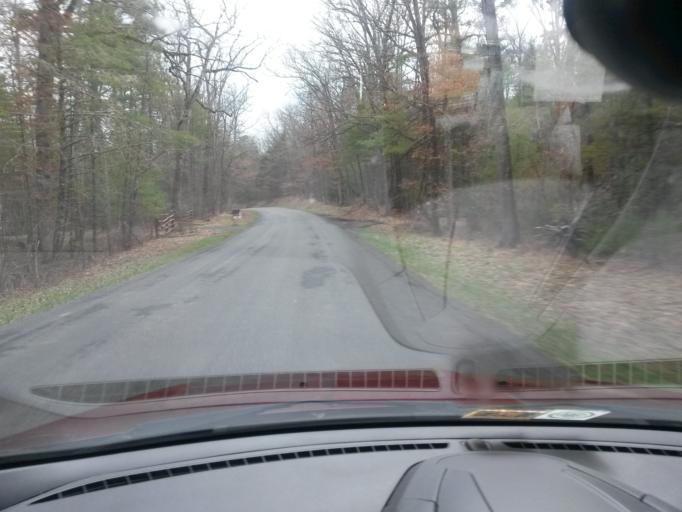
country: US
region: Virginia
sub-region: Bath County
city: Warm Springs
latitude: 38.0733
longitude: -79.8252
